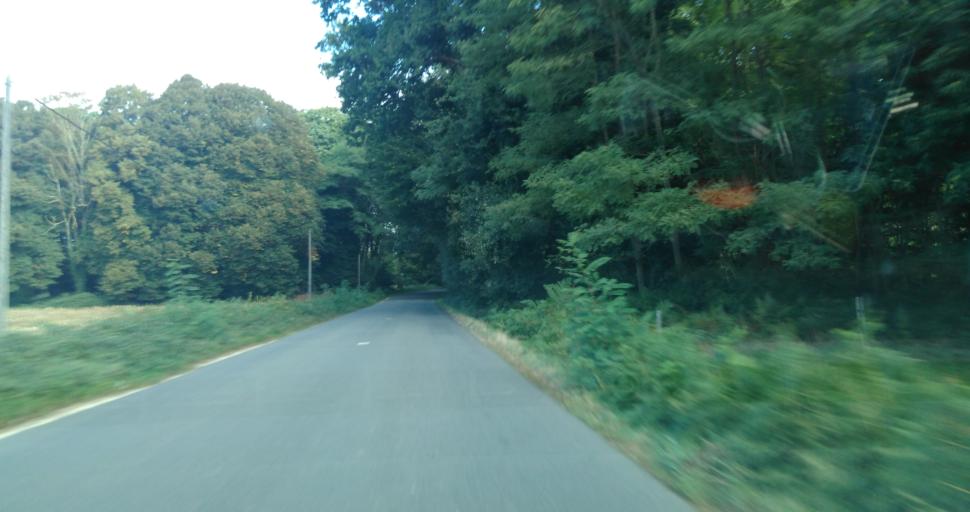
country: FR
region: Brittany
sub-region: Departement d'Ille-et-Vilaine
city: Iffendic
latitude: 48.1589
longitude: -2.0136
